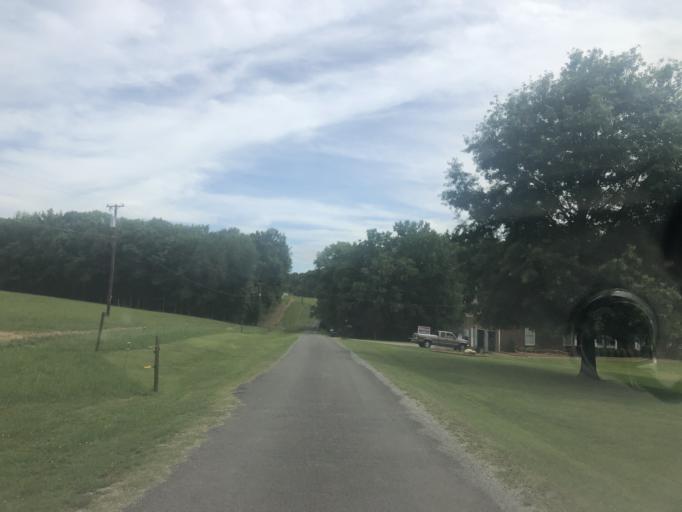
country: US
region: Tennessee
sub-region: Davidson County
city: Lakewood
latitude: 36.2189
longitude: -86.6617
